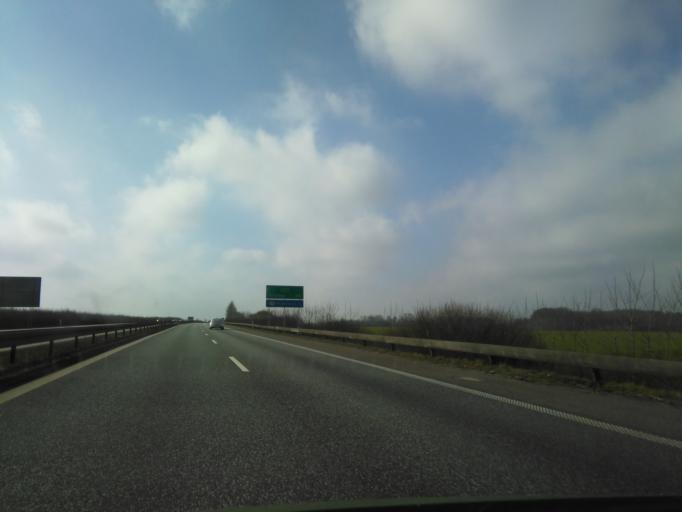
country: DK
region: Central Jutland
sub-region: Hedensted Kommune
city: Hedensted
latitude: 55.8380
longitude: 9.7267
